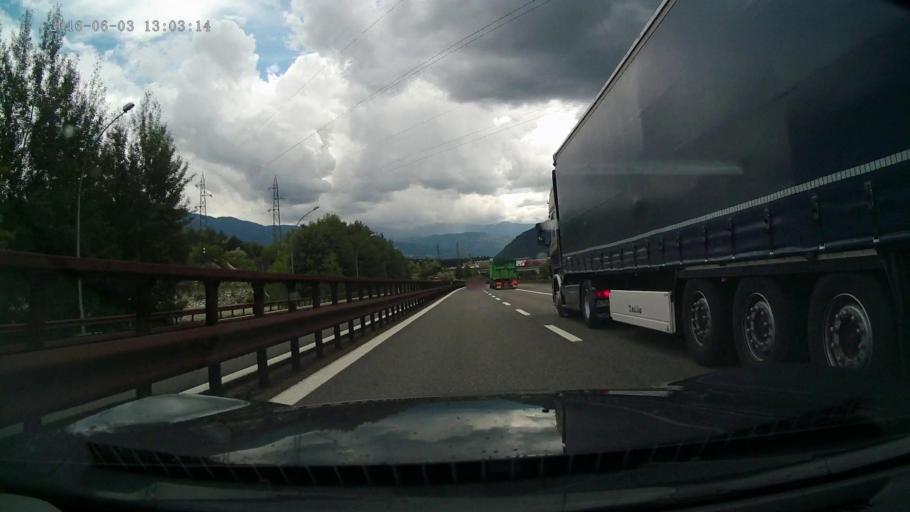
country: IT
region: Trentino-Alto Adige
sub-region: Bolzano
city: Varna
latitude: 46.7658
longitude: 11.6386
